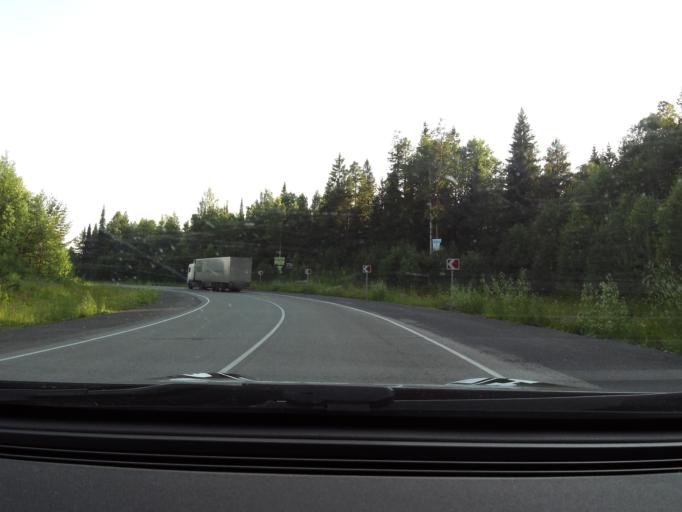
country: RU
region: Sverdlovsk
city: Druzhinino
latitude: 56.8007
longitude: 59.4639
